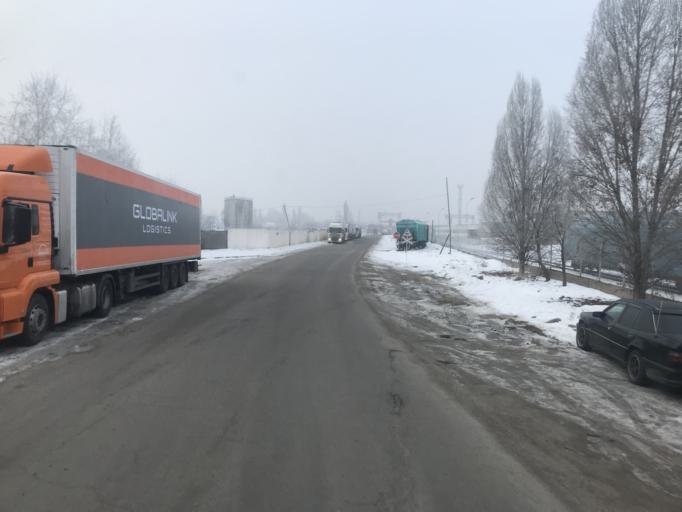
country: KZ
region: Almaty Oblysy
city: Pervomayskiy
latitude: 43.3607
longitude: 76.9772
